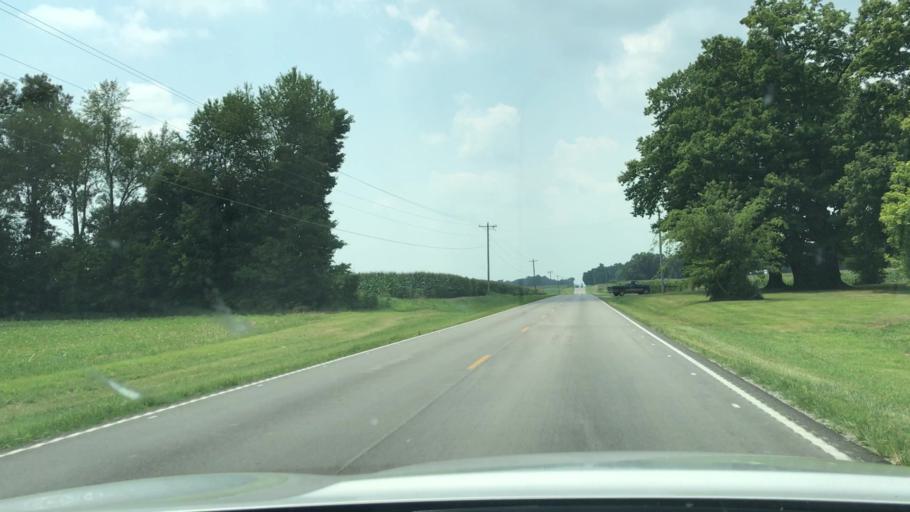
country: US
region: Kentucky
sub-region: Todd County
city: Guthrie
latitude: 36.6957
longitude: -87.1236
